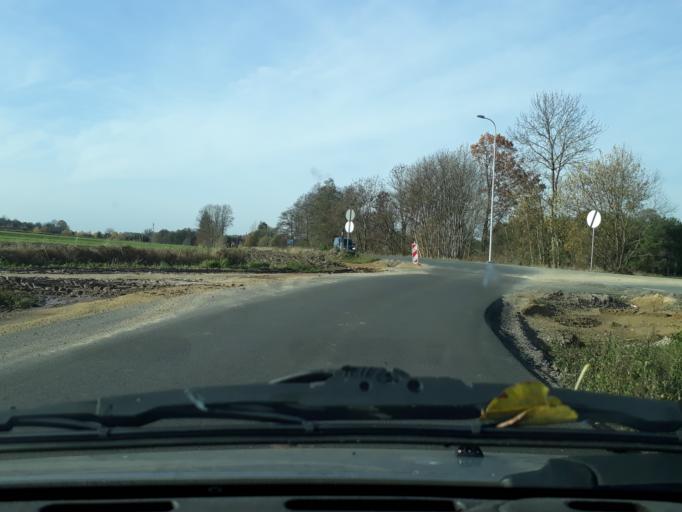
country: PL
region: Silesian Voivodeship
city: Wozniki
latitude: 50.5906
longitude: 19.0853
